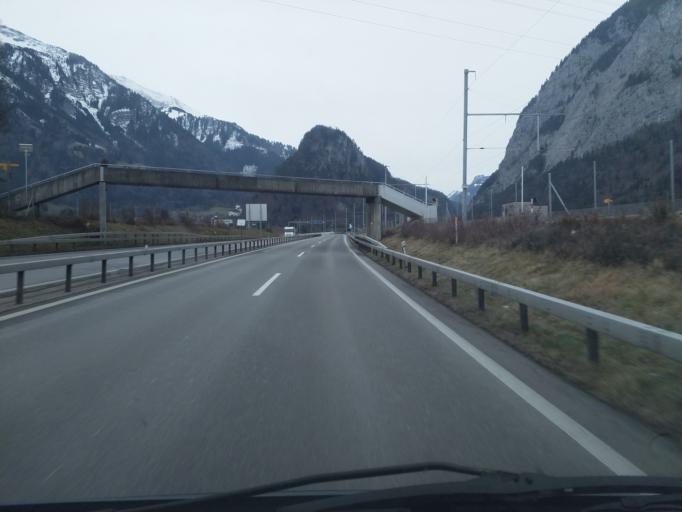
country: CH
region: Bern
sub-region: Frutigen-Niedersimmental District
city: Wimmis
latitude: 46.6843
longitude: 7.6433
